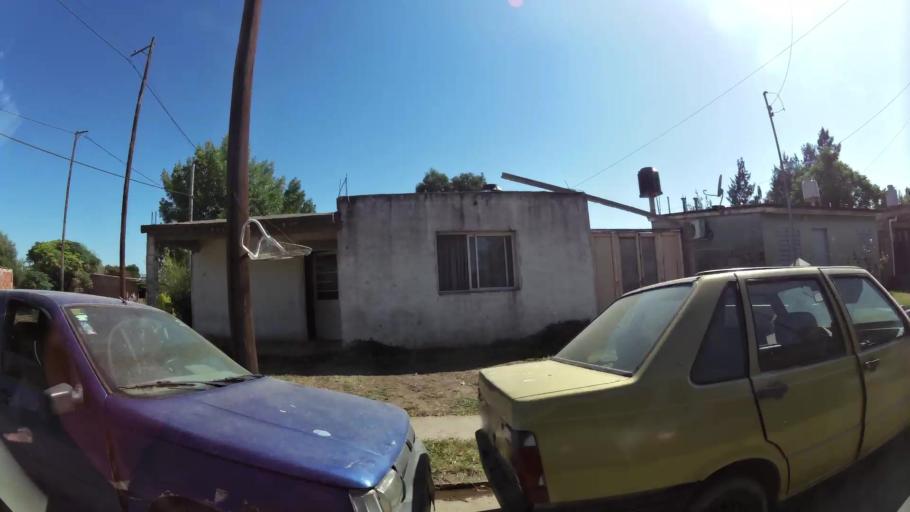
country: AR
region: Cordoba
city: Villa Allende
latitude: -31.3200
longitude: -64.2511
